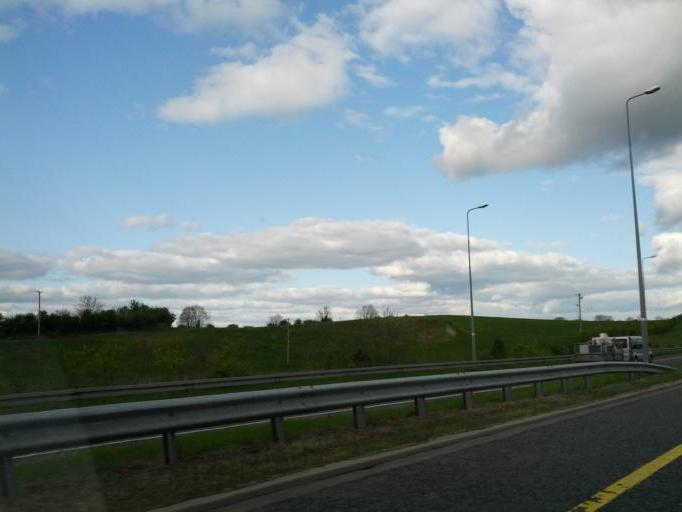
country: IE
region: Leinster
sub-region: An Iarmhi
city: Kilbeggan
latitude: 53.3583
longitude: -7.4906
